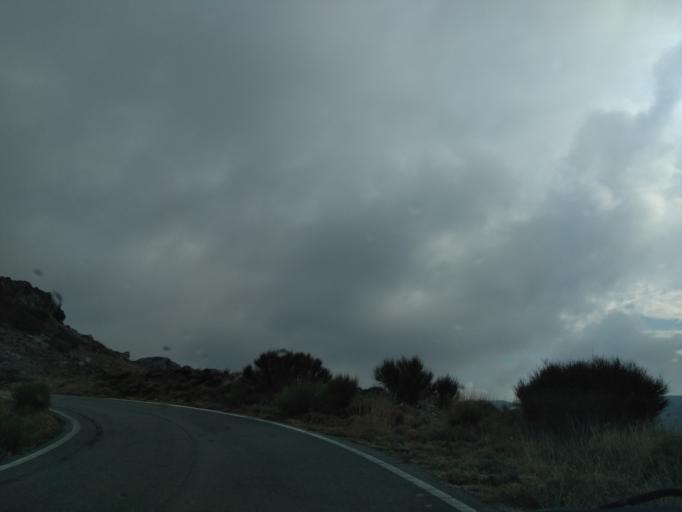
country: GR
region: Crete
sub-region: Nomos Lasithiou
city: Siteia
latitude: 35.1531
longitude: 26.0177
